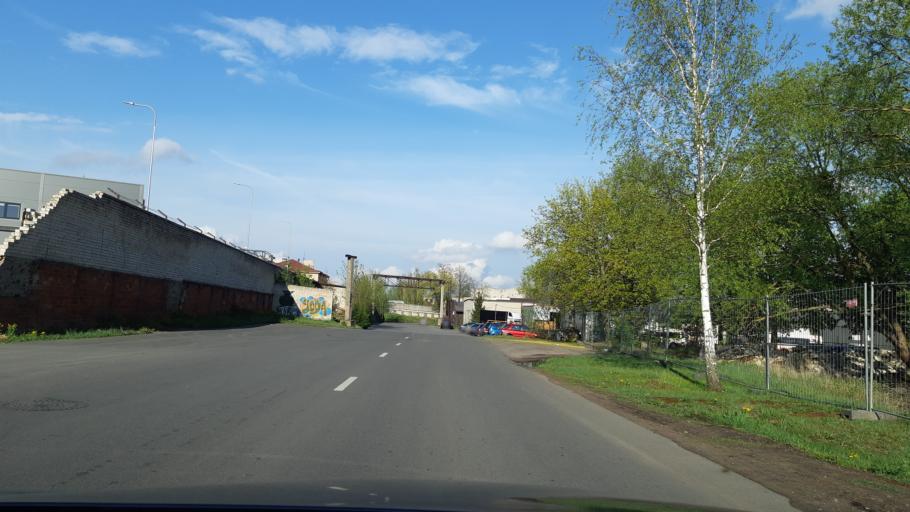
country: LT
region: Kauno apskritis
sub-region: Kaunas
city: Aleksotas
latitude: 54.8626
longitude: 23.9442
